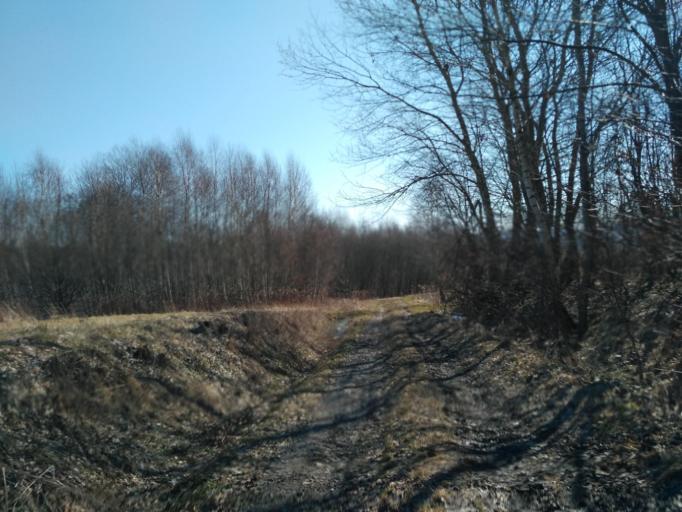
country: PL
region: Subcarpathian Voivodeship
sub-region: Powiat brzozowski
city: Domaradz
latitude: 49.7953
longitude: 21.9763
